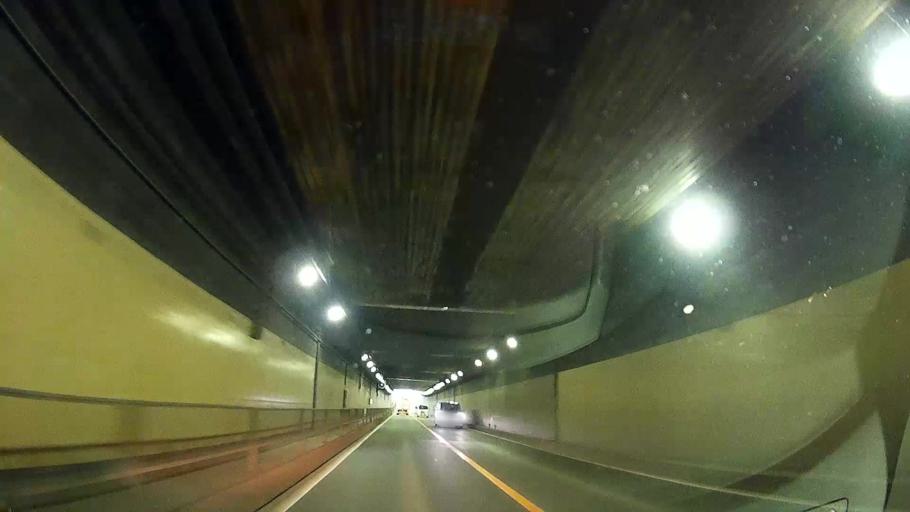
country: JP
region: Kumamoto
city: Ozu
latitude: 32.8369
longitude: 130.8540
